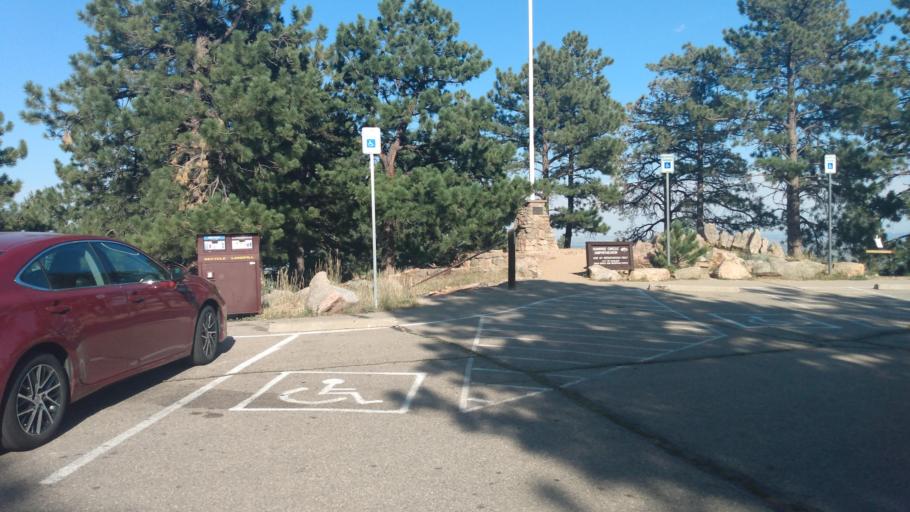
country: US
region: Colorado
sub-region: Boulder County
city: Boulder
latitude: 40.0037
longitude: -105.3015
